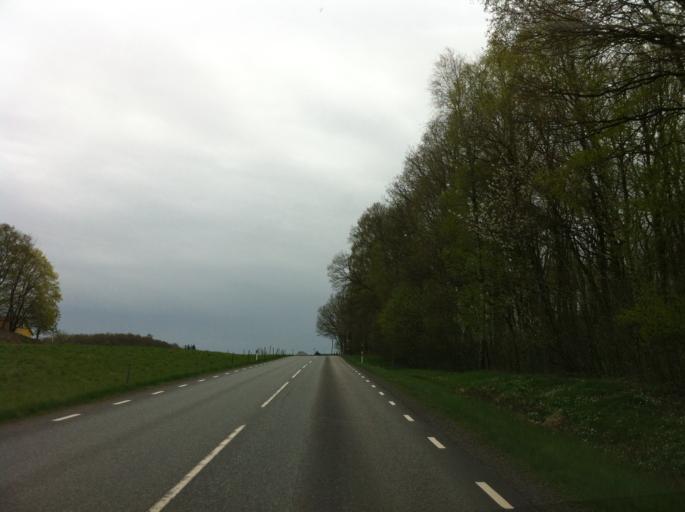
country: SE
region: Halland
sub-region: Falkenbergs Kommun
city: Falkenberg
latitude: 57.0356
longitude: 12.5996
